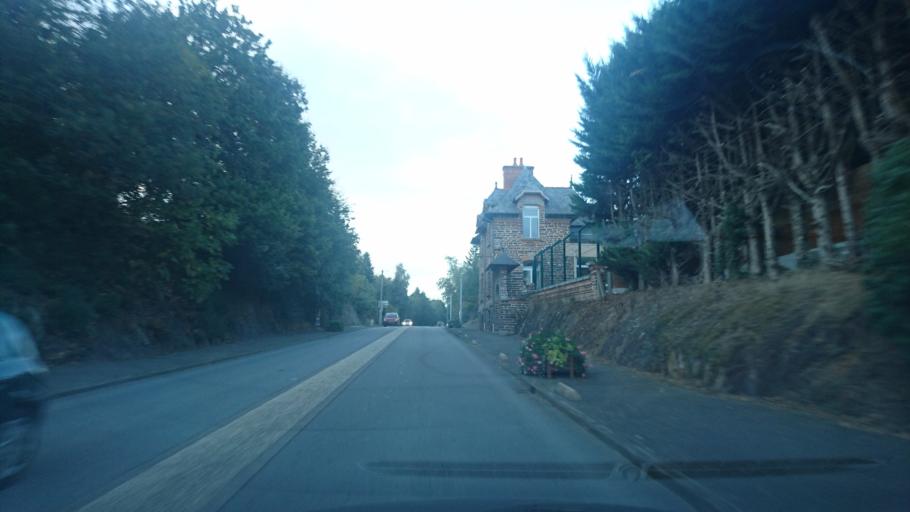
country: FR
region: Brittany
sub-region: Departement d'Ille-et-Vilaine
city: Baulon
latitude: 47.9297
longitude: -1.9417
